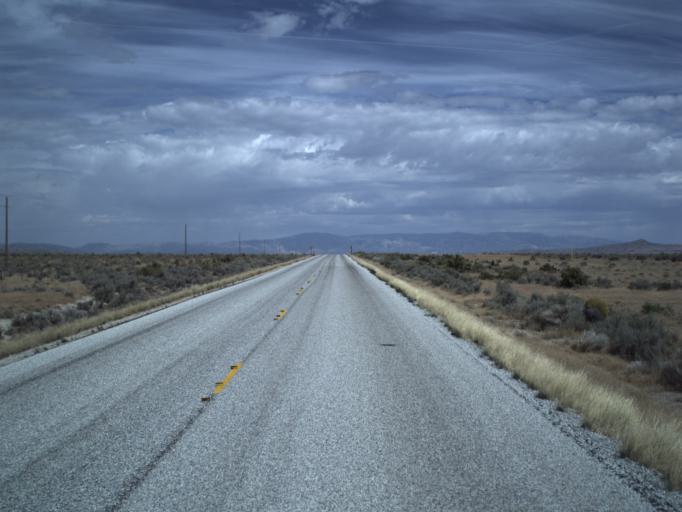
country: US
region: Utah
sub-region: Tooele County
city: Wendover
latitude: 41.5384
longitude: -113.5911
